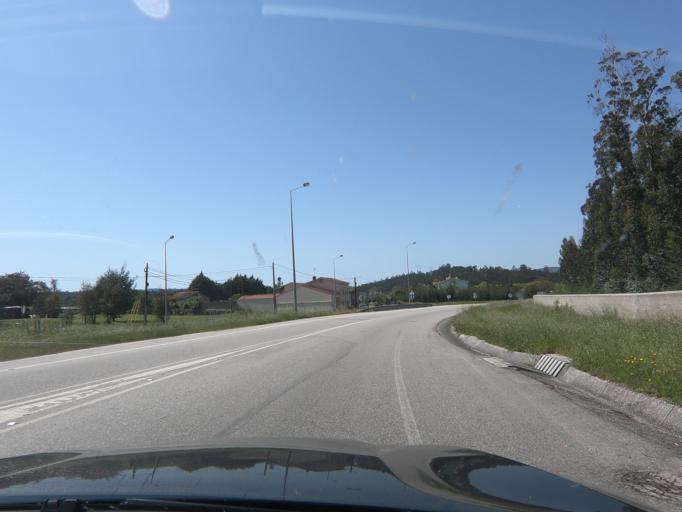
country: PT
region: Coimbra
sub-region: Lousa
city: Lousa
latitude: 40.1366
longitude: -8.2508
